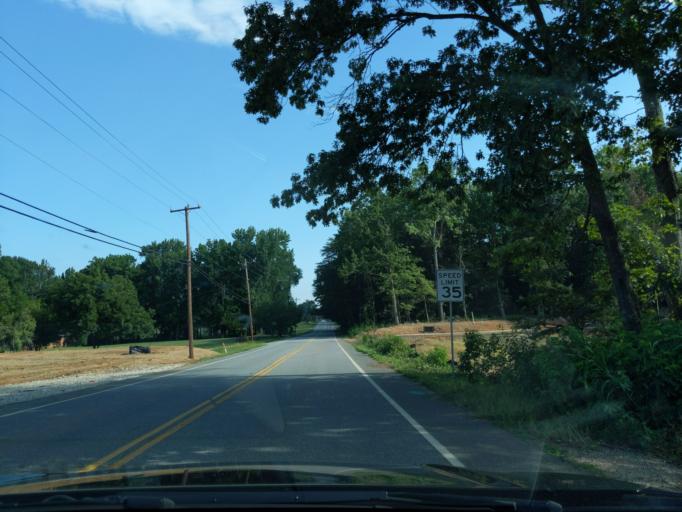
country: US
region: South Carolina
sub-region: Greenville County
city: Mauldin
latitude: 34.8119
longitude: -82.3112
